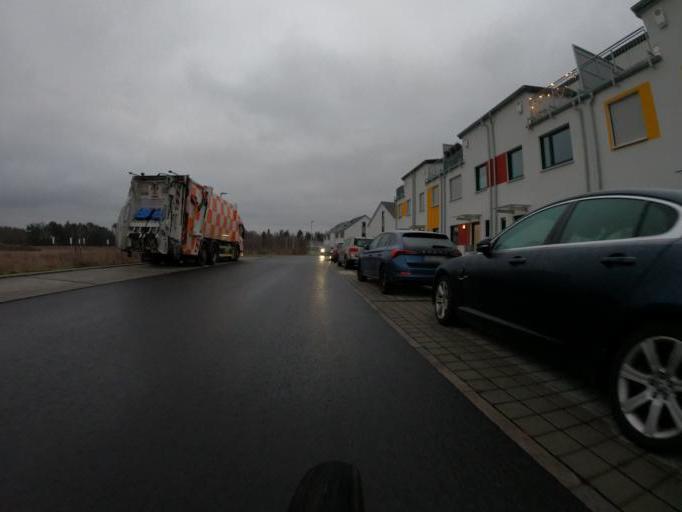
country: DE
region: Brandenburg
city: Schulzendorf
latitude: 52.3577
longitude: 13.5813
